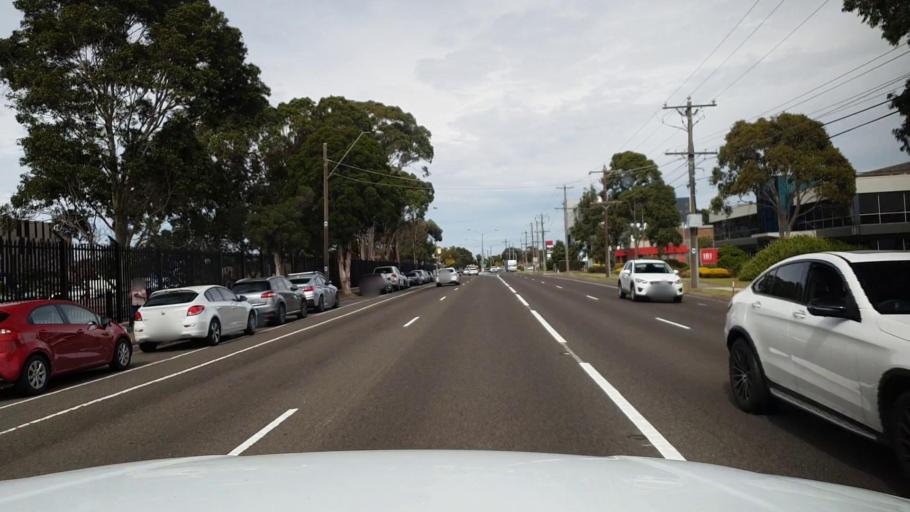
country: AU
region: Victoria
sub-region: Monash
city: Notting Hill
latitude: -37.8971
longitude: 145.1297
